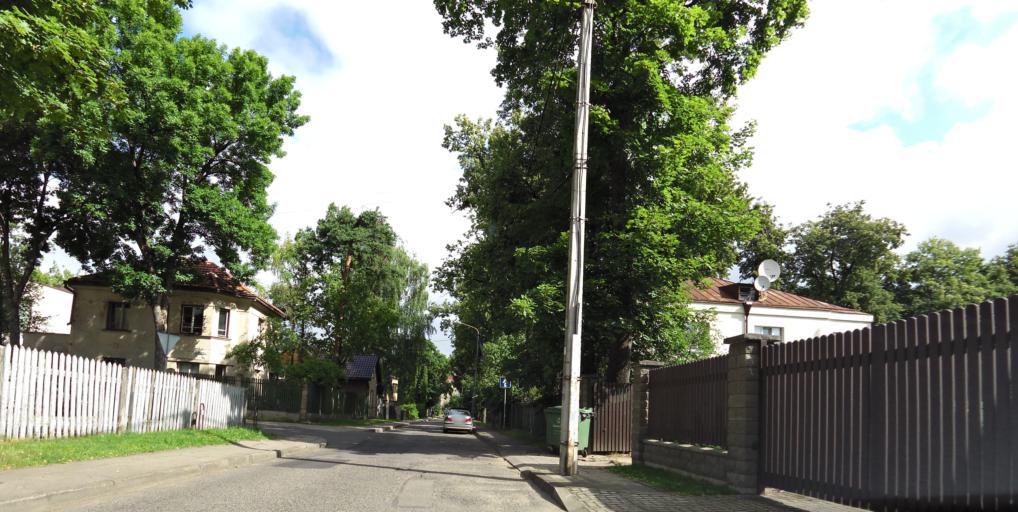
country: LT
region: Vilnius County
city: Seskine
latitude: 54.6936
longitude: 25.2575
